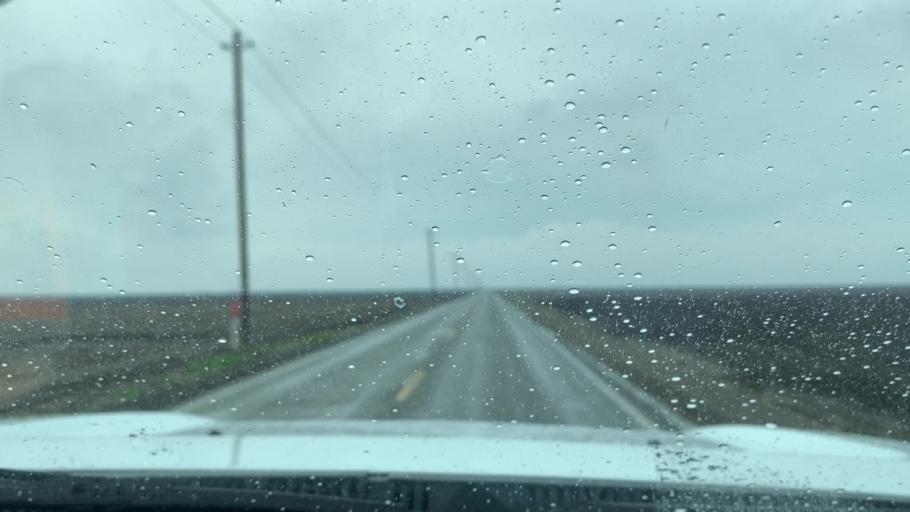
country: US
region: California
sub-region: Tulare County
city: Alpaugh
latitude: 35.9729
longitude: -119.5720
